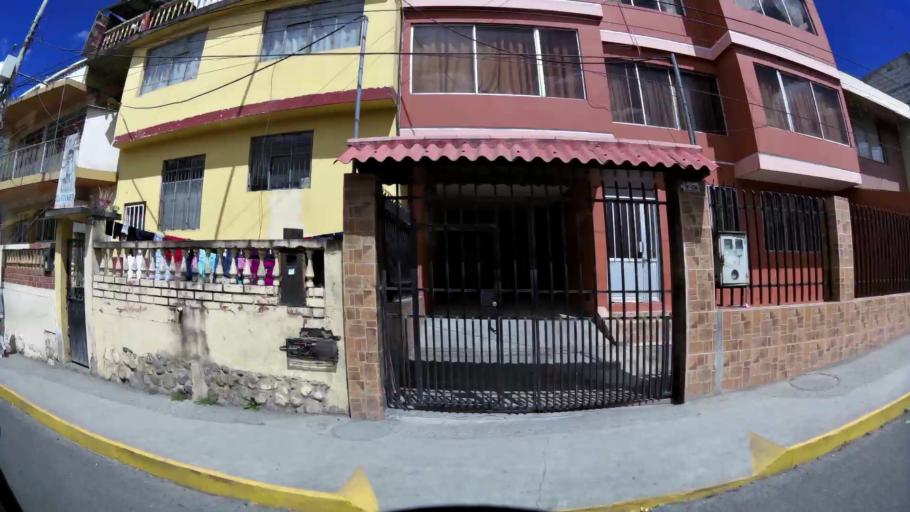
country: EC
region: Canar
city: Azogues
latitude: -2.7384
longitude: -78.8494
